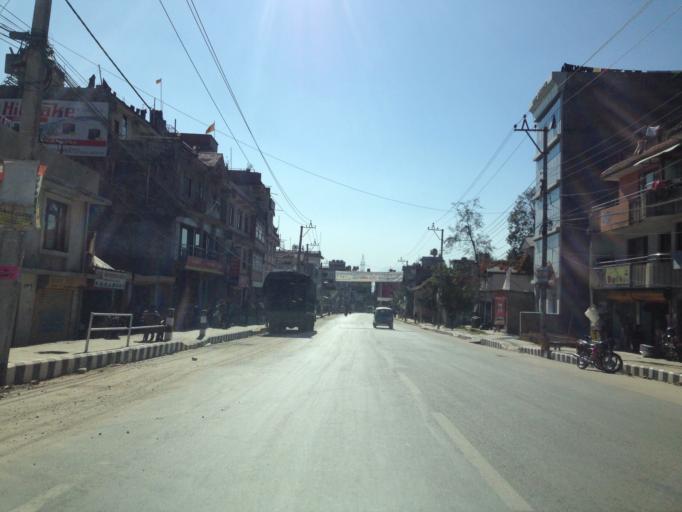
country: NP
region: Central Region
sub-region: Bagmati Zone
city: Kathmandu
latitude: 27.7693
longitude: 85.3571
